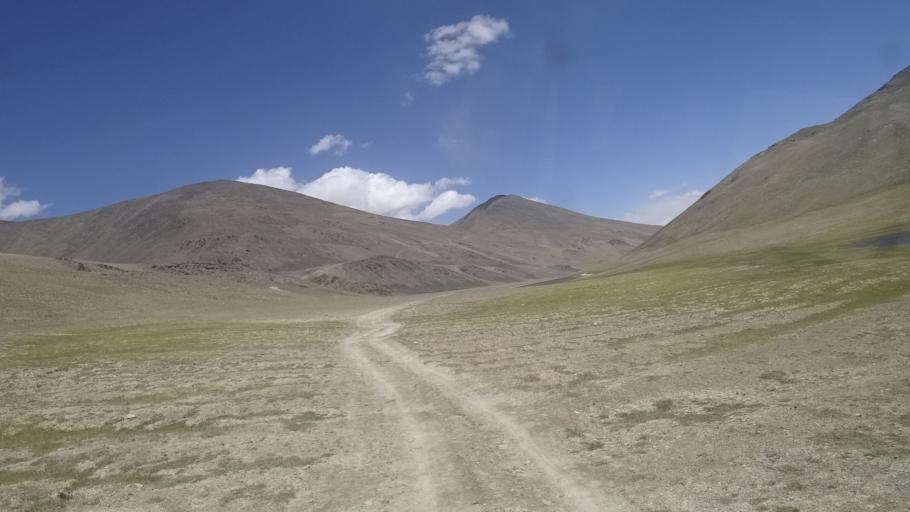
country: TJ
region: Gorno-Badakhshan
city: Murghob
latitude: 37.5178
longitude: 74.0583
